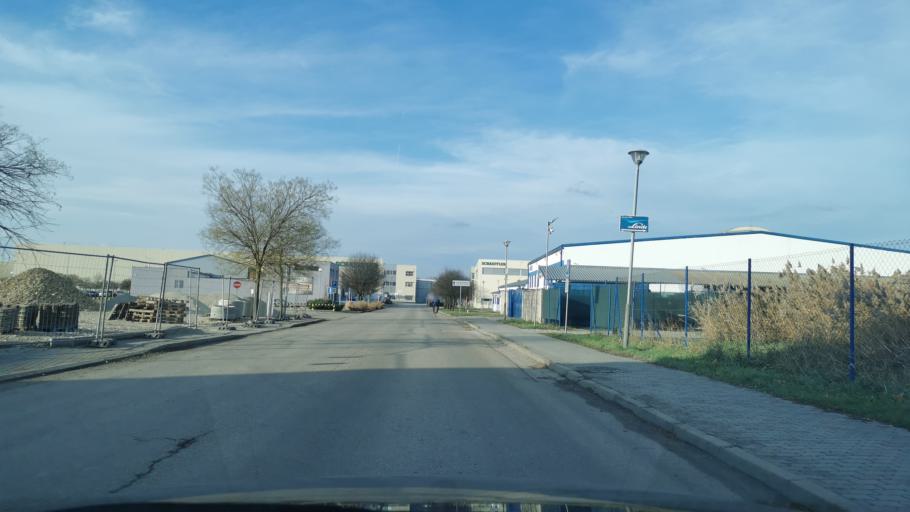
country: SK
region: Trnavsky
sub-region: Okres Skalica
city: Skalica
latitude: 48.8486
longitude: 17.2146
